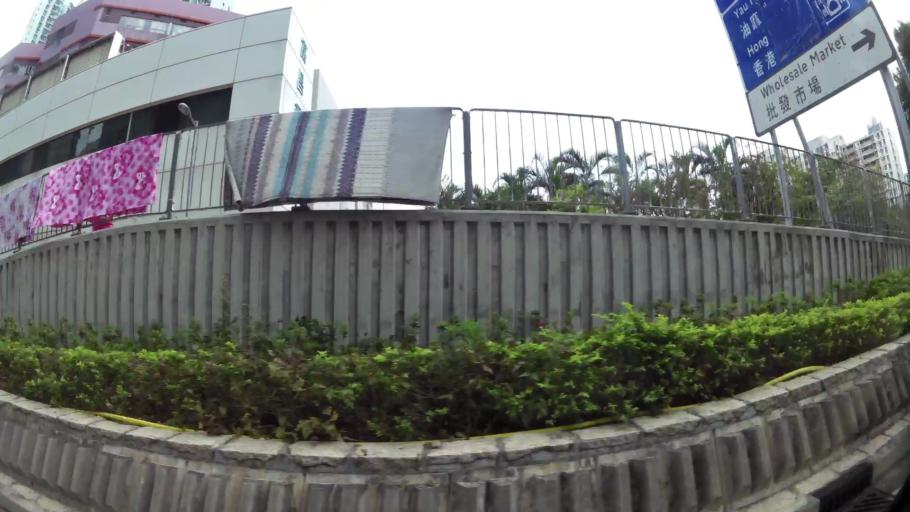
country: HK
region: Sham Shui Po
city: Sham Shui Po
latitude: 22.3267
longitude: 114.1554
